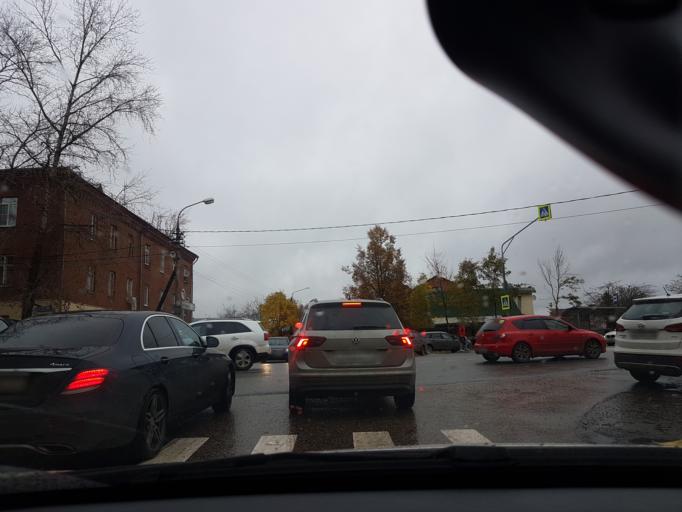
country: RU
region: Moskovskaya
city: Istra
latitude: 55.9196
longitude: 36.8688
